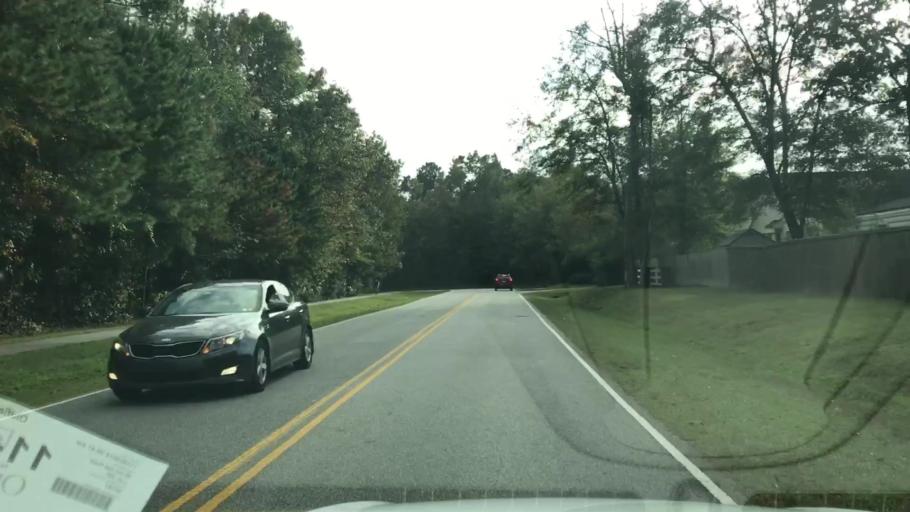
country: US
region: South Carolina
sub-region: Berkeley County
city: Sangaree
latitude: 33.0260
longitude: -80.1101
